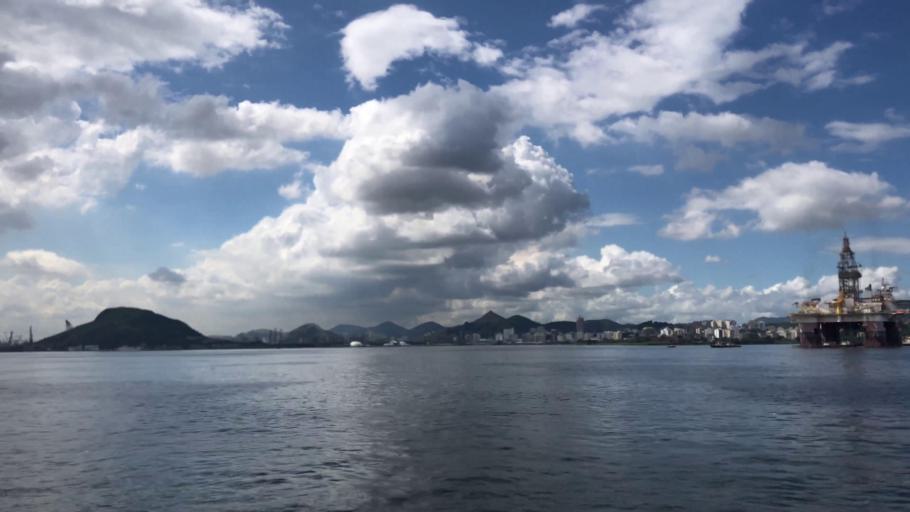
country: BR
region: Rio de Janeiro
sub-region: Niteroi
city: Niteroi
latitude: -22.8964
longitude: -43.1478
